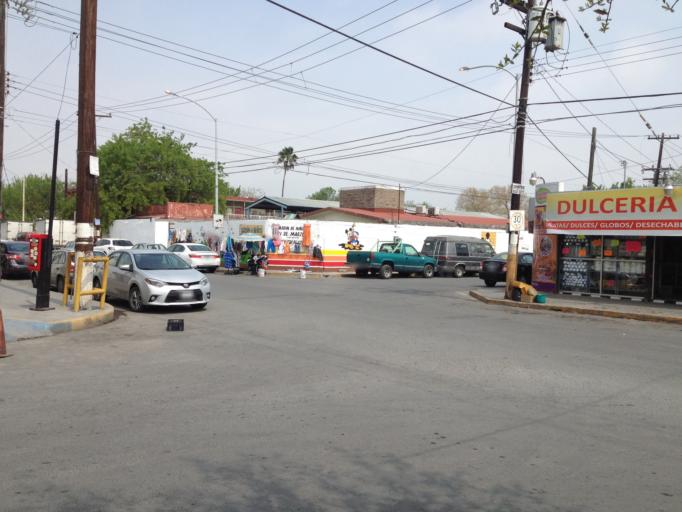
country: MX
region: Nuevo Leon
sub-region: Monterrey
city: Monterrey
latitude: 25.6628
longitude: -100.2872
